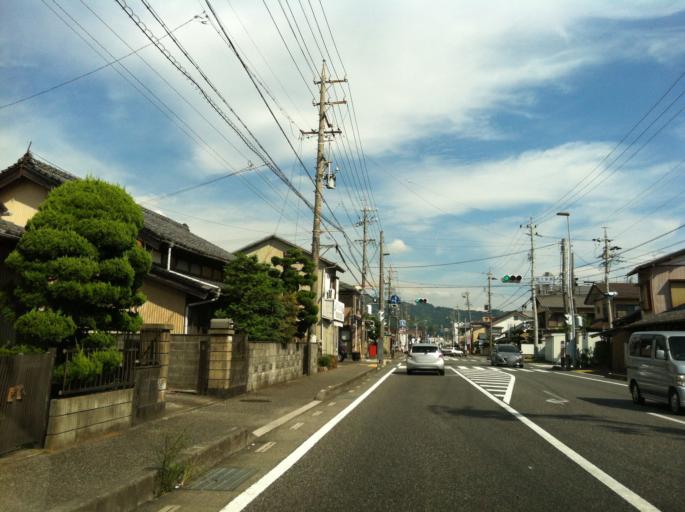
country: JP
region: Shizuoka
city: Shizuoka-shi
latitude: 35.0318
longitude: 138.4894
